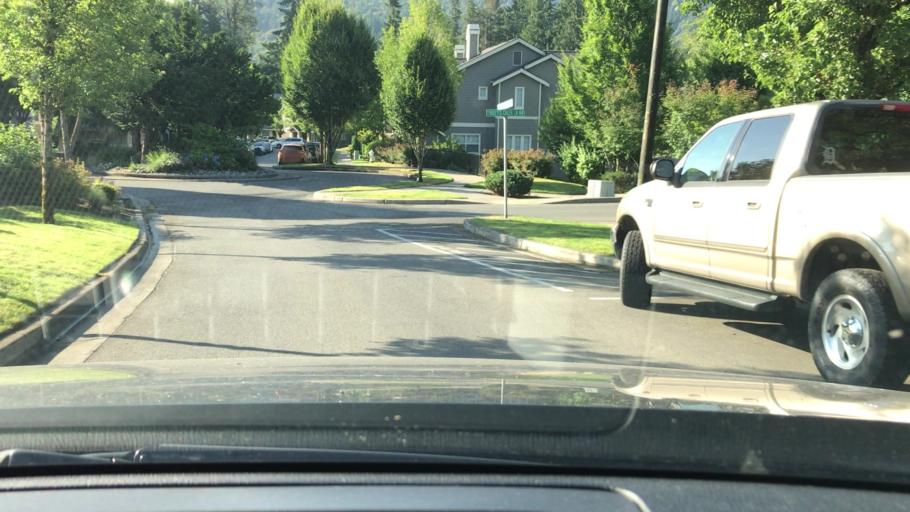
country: US
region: Washington
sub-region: King County
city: Issaquah
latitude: 47.5310
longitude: -122.0719
